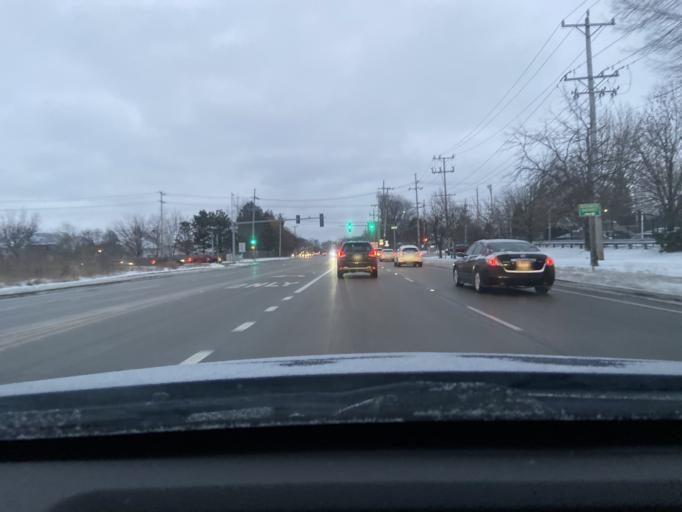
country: US
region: Illinois
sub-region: Lake County
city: Grayslake
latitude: 42.3570
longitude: -88.0449
